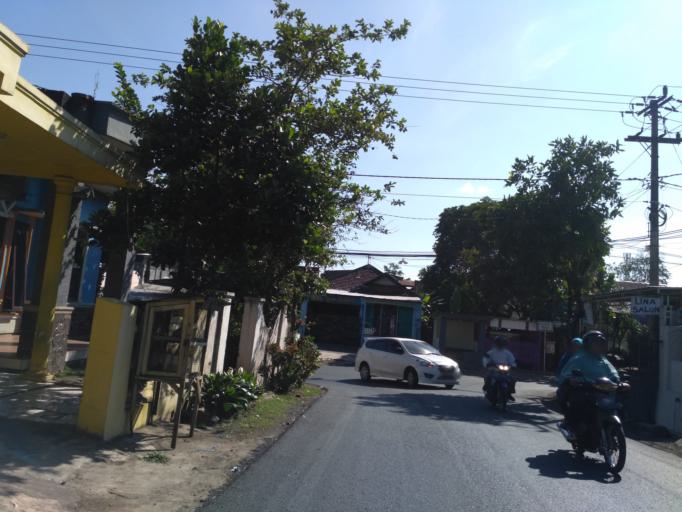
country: ID
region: East Java
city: Singosari
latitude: -7.9175
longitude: 112.6650
